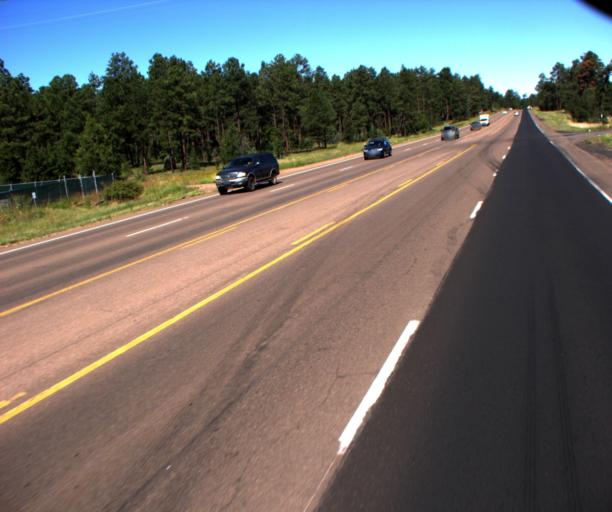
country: US
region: Arizona
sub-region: Navajo County
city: Lake of the Woods
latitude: 34.1752
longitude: -110.0070
